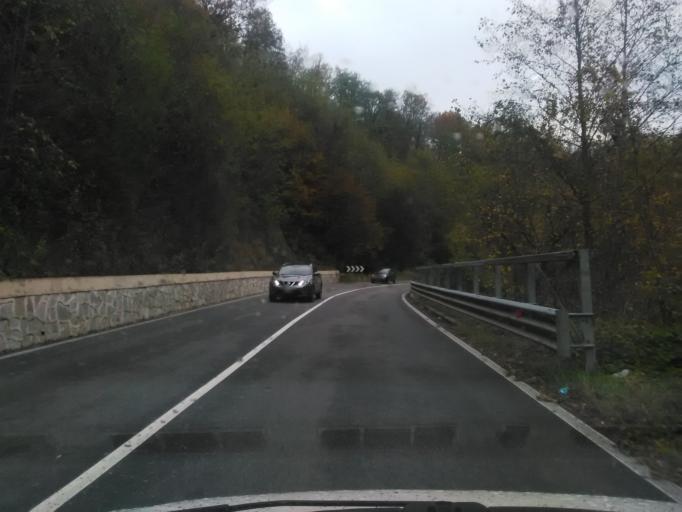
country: IT
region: Piedmont
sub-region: Provincia di Vercelli
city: Borgosesia
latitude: 45.7154
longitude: 8.2976
